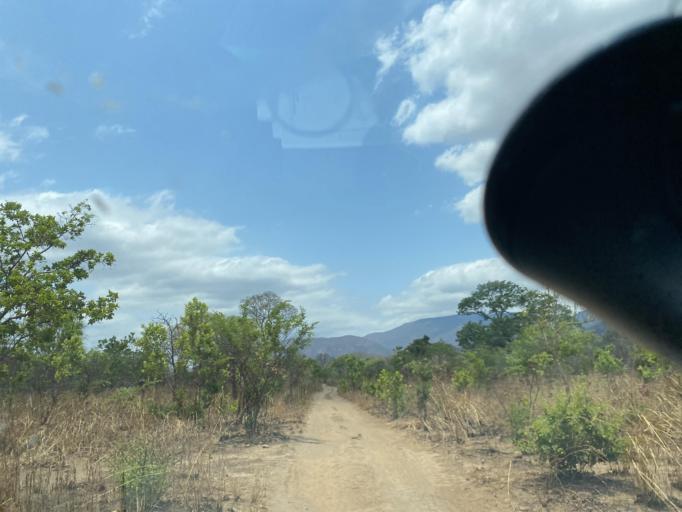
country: ZM
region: Lusaka
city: Luangwa
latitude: -15.1828
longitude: 29.7271
